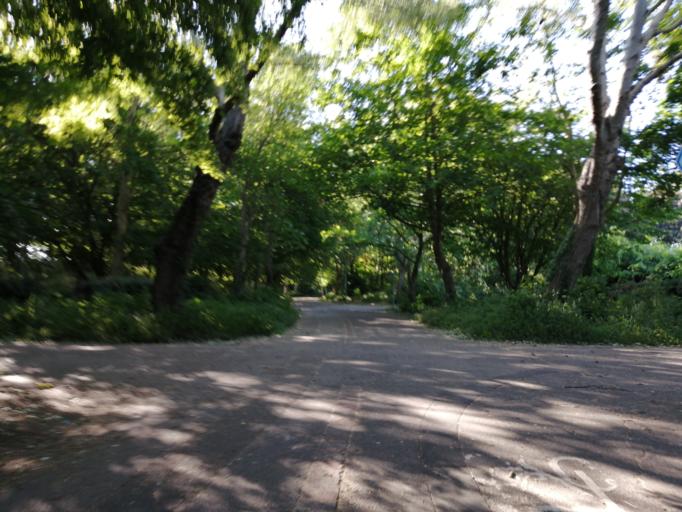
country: GB
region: England
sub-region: Peterborough
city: Marholm
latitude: 52.5968
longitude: -0.2763
